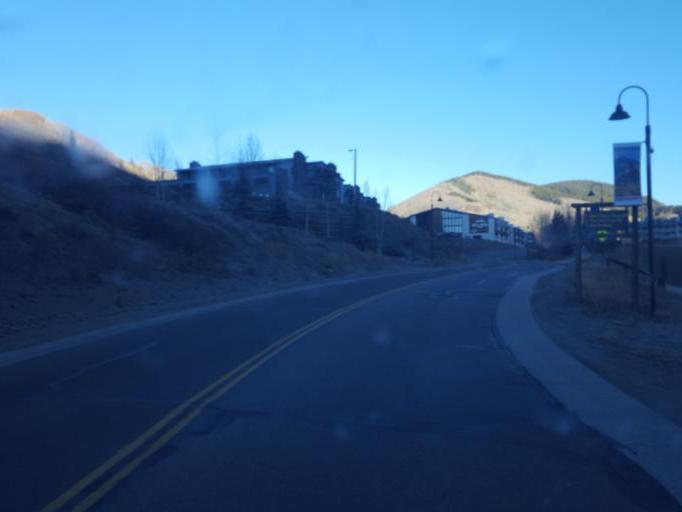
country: US
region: Colorado
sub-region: Gunnison County
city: Crested Butte
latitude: 38.9011
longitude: -106.9687
